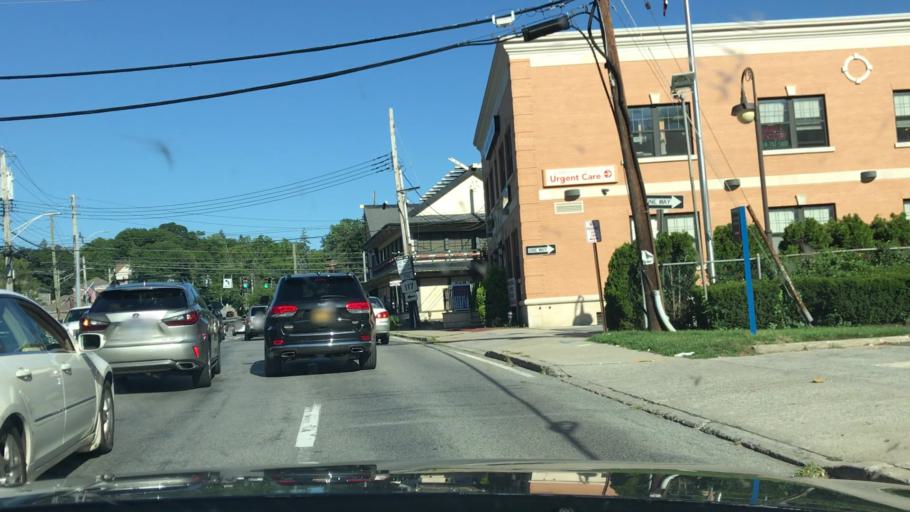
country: US
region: New York
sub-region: Westchester County
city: Thornwood
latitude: 41.1240
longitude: -73.7820
